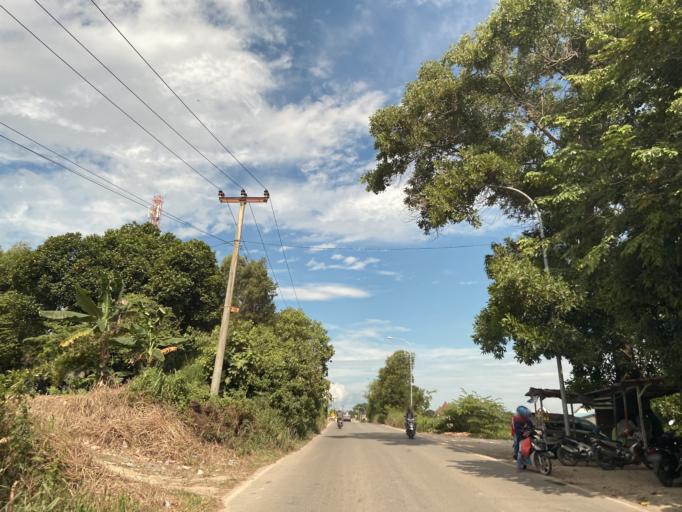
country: SG
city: Singapore
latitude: 1.0330
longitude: 103.9401
